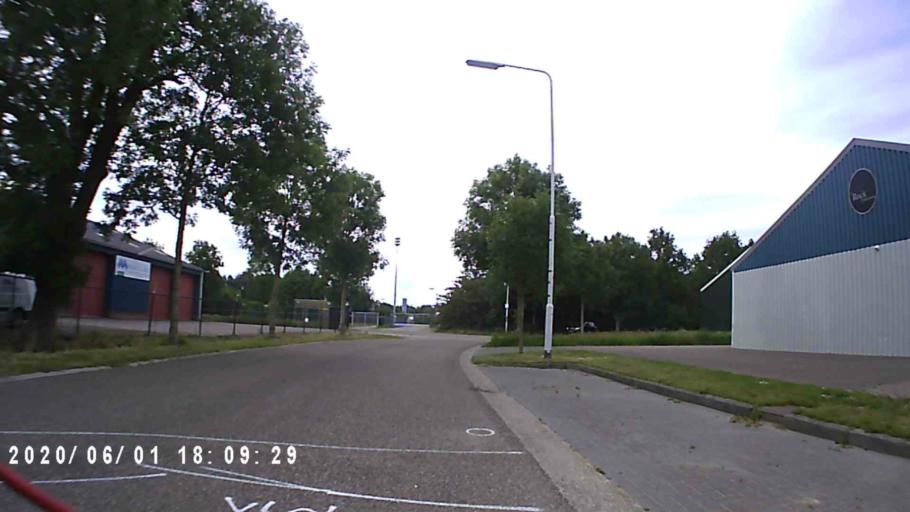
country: NL
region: Friesland
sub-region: Gemeente Tytsjerksteradiel
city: Sumar
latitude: 53.1833
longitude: 6.0050
